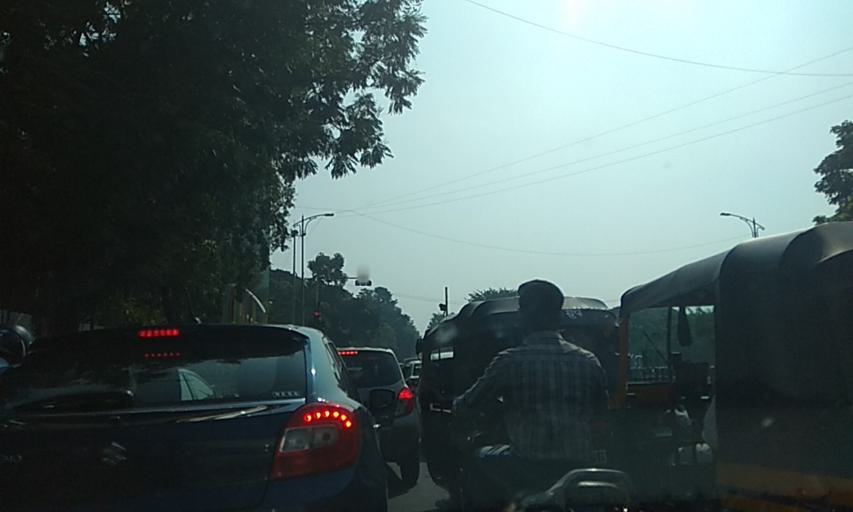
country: IN
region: Maharashtra
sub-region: Pune Division
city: Shivaji Nagar
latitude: 18.5453
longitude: 73.8765
